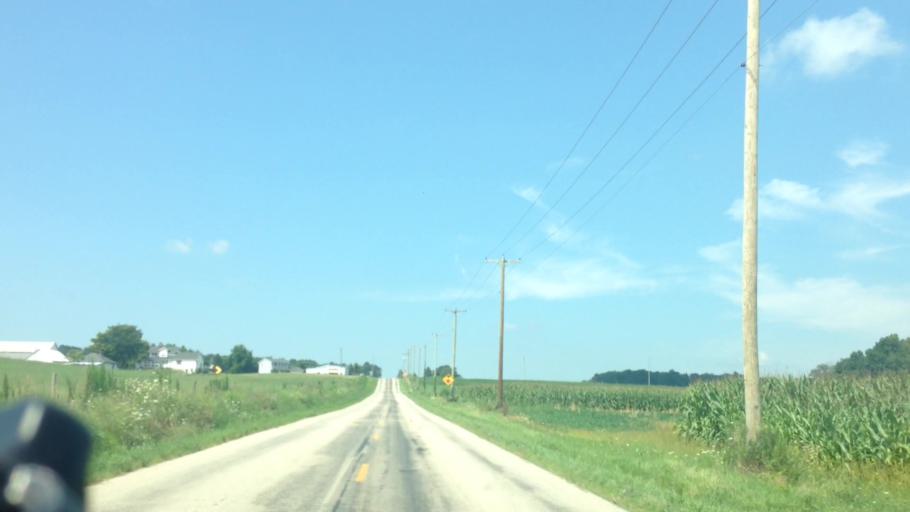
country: US
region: Ohio
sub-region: Wayne County
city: Orrville
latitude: 40.8739
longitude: -81.7995
